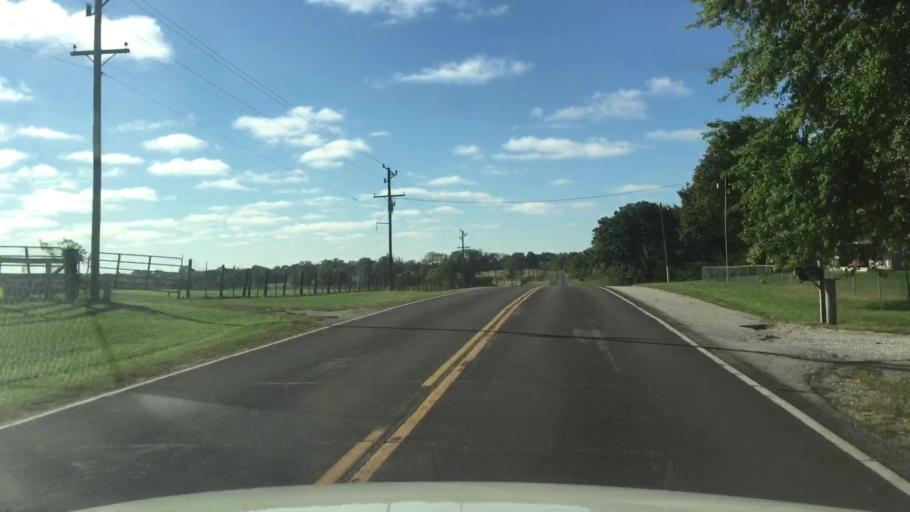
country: US
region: Missouri
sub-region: Howard County
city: New Franklin
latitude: 39.0461
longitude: -92.7445
